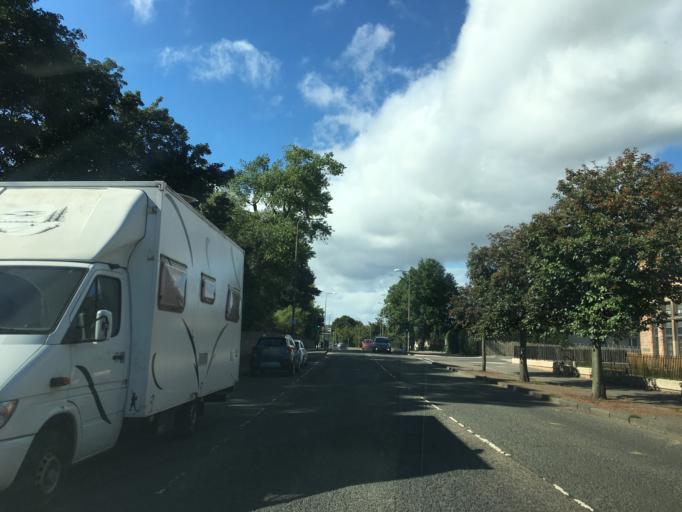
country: GB
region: Scotland
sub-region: West Lothian
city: Seafield
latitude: 55.9340
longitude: -3.1183
